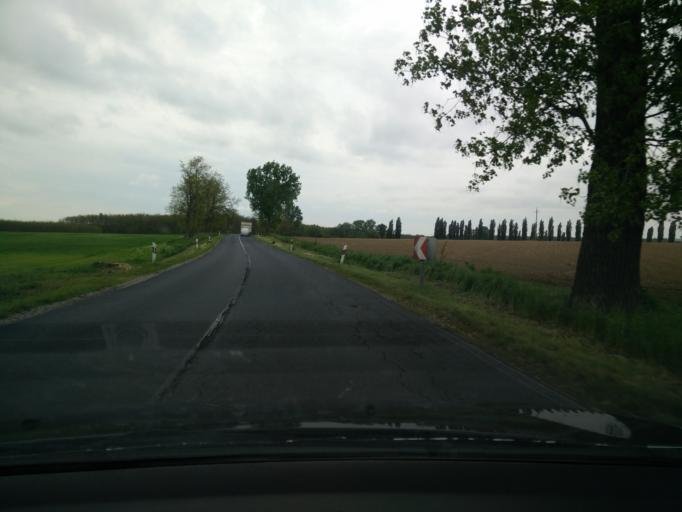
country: HU
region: Gyor-Moson-Sopron
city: Tet
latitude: 47.5343
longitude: 17.5322
